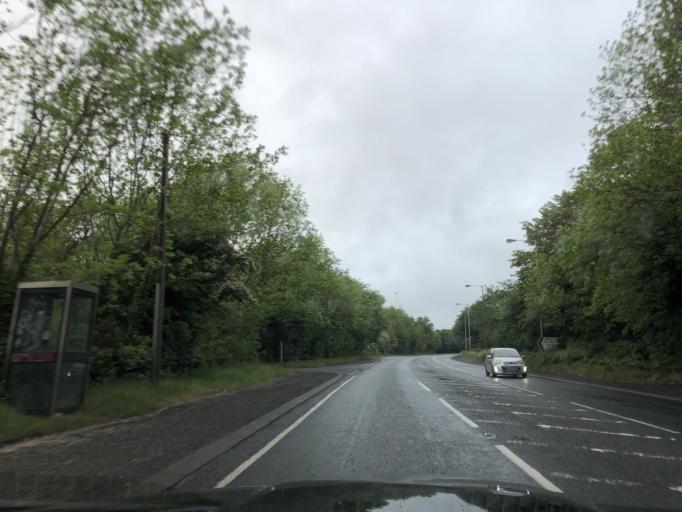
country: GB
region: Northern Ireland
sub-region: Antrim Borough
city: Antrim
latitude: 54.7416
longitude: -6.2345
